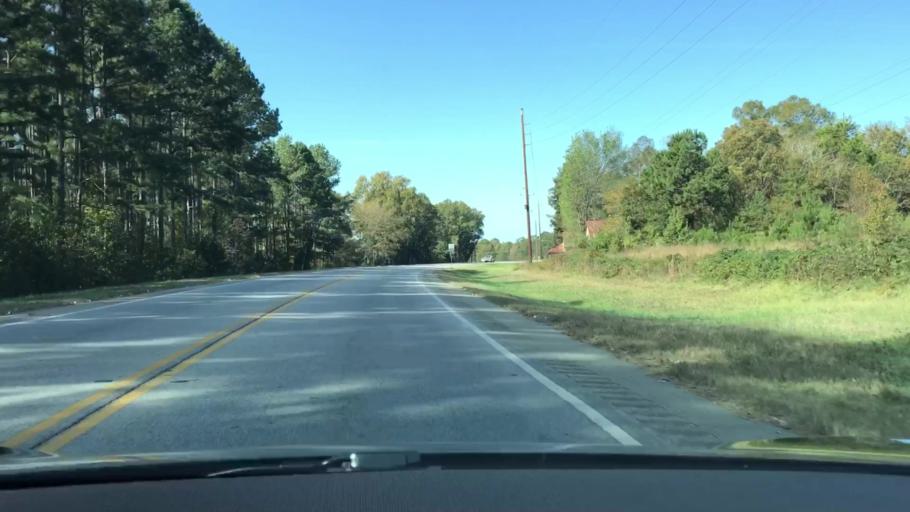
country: US
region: Georgia
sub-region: Warren County
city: Warrenton
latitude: 33.4000
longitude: -82.6634
